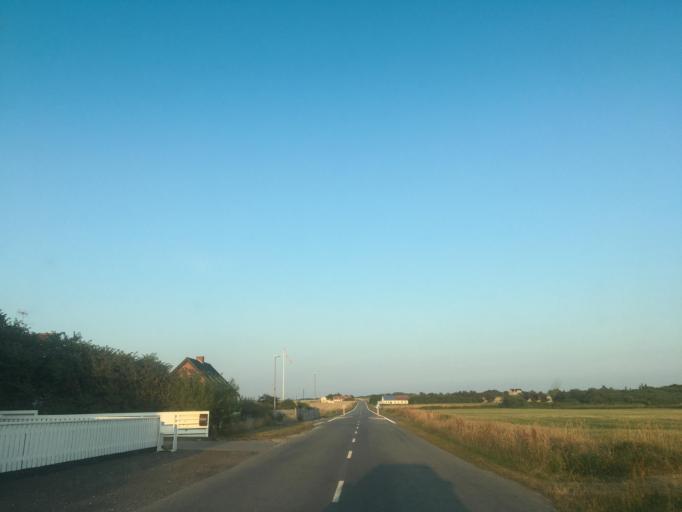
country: DK
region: Central Jutland
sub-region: Lemvig Kommune
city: Thyboron
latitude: 56.7690
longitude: 8.2851
